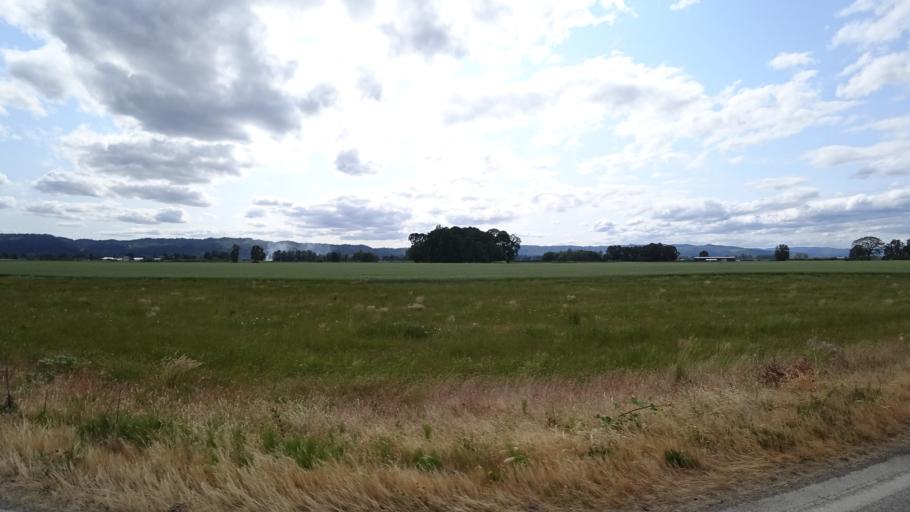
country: US
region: Washington
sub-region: Clark County
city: Felida
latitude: 45.6542
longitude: -122.7791
